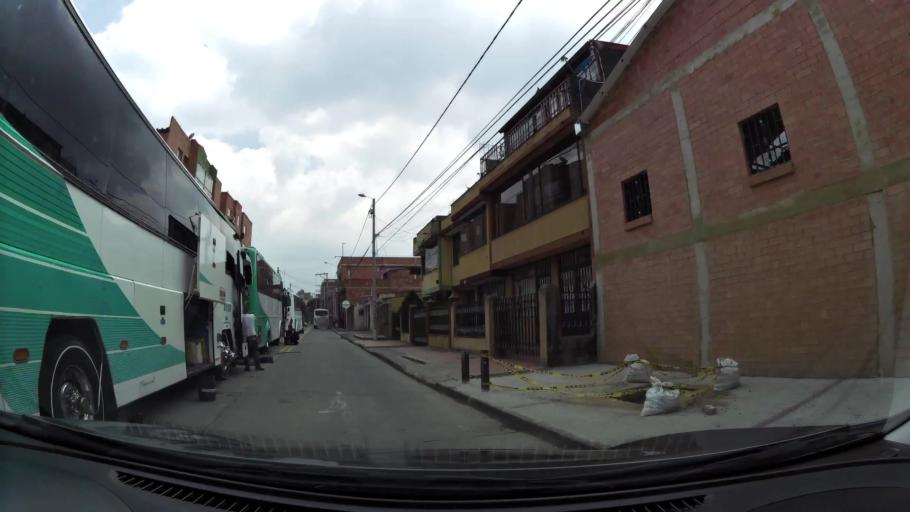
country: CO
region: Cundinamarca
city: La Calera
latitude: 4.7302
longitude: -74.0263
